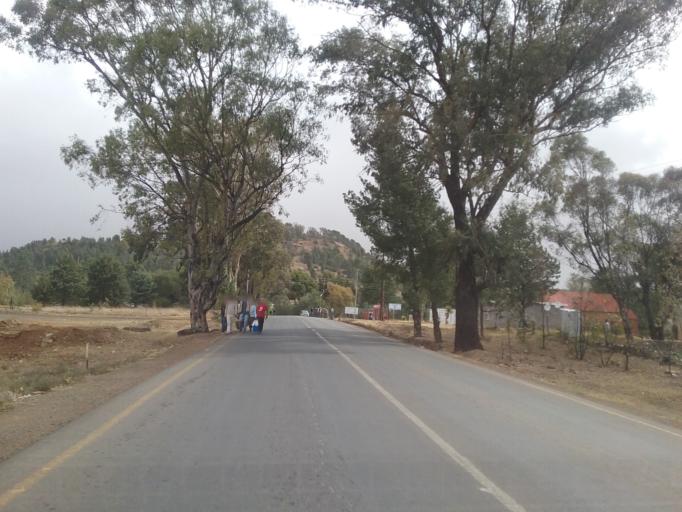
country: LS
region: Quthing
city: Quthing
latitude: -30.4048
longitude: 27.7085
